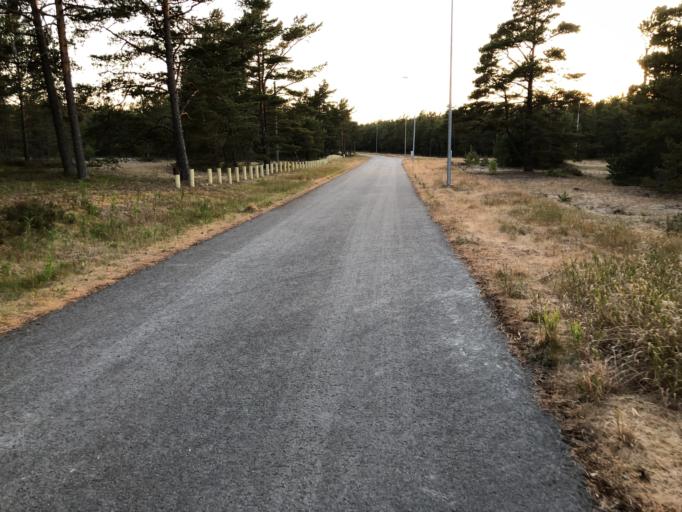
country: EE
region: Harju
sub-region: Paldiski linn
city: Paldiski
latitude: 59.3920
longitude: 24.2320
